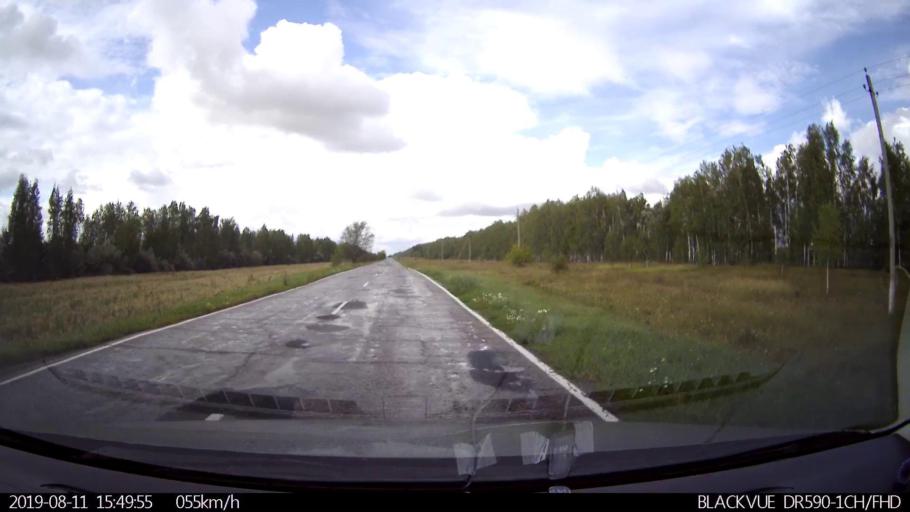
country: RU
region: Ulyanovsk
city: Ignatovka
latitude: 53.9082
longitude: 47.6556
